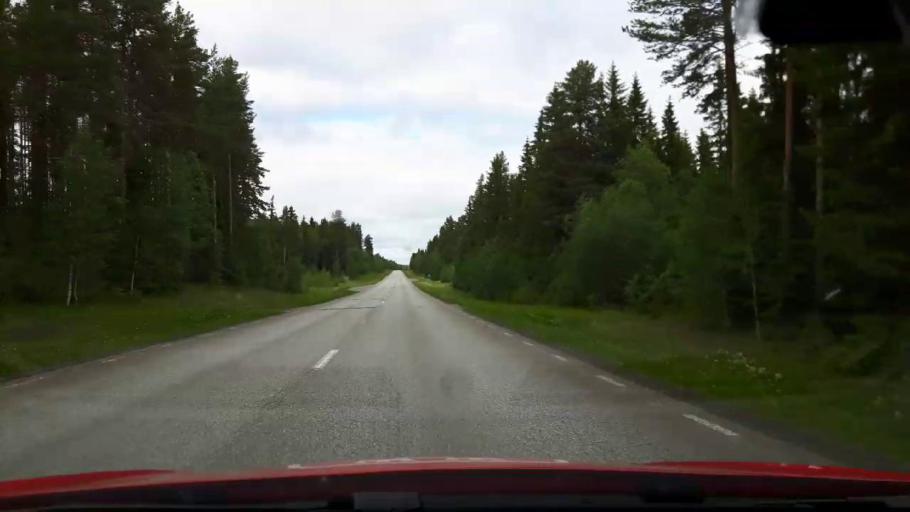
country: SE
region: Jaemtland
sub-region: Krokoms Kommun
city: Krokom
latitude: 63.4409
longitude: 14.4955
